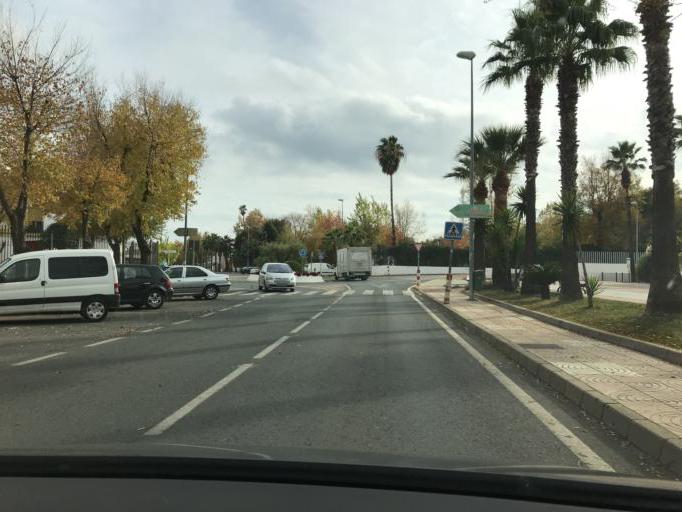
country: ES
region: Andalusia
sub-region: Provincia de Sevilla
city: La Campana
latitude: 37.5675
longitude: -5.4290
